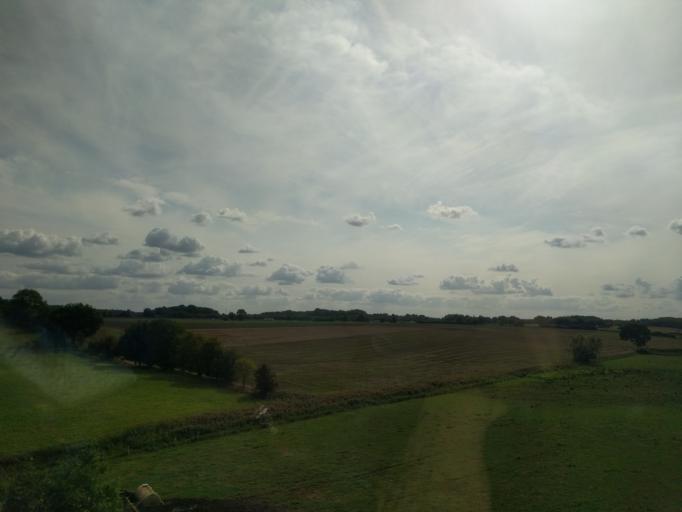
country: DE
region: Schleswig-Holstein
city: Wesenberg
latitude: 53.8344
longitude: 10.5450
